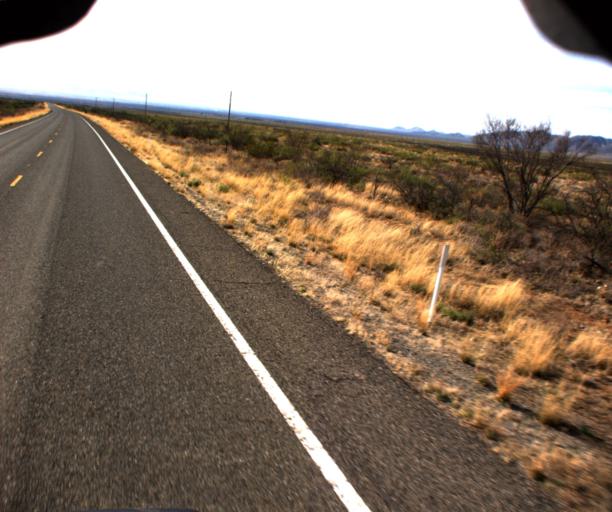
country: US
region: Arizona
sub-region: Cochise County
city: Willcox
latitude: 32.1861
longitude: -109.6767
